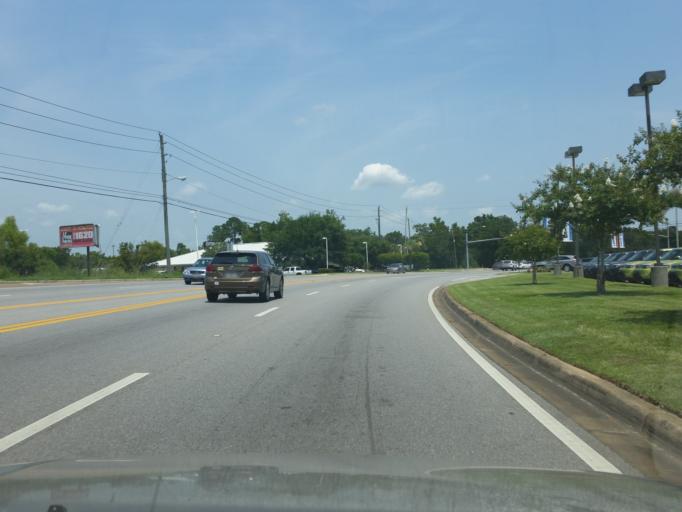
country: US
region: Florida
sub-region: Escambia County
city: Brent
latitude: 30.4852
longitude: -87.2598
